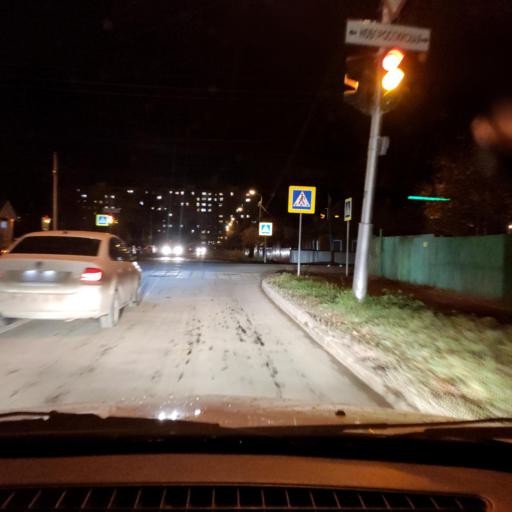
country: RU
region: Bashkortostan
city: Avdon
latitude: 54.7086
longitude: 55.8203
